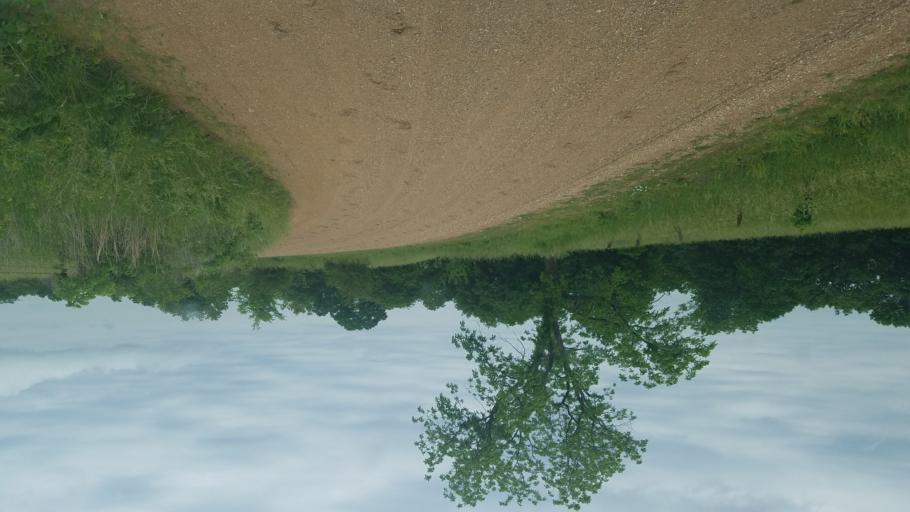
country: US
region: Missouri
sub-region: Moniteau County
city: Tipton
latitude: 38.5491
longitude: -92.7470
